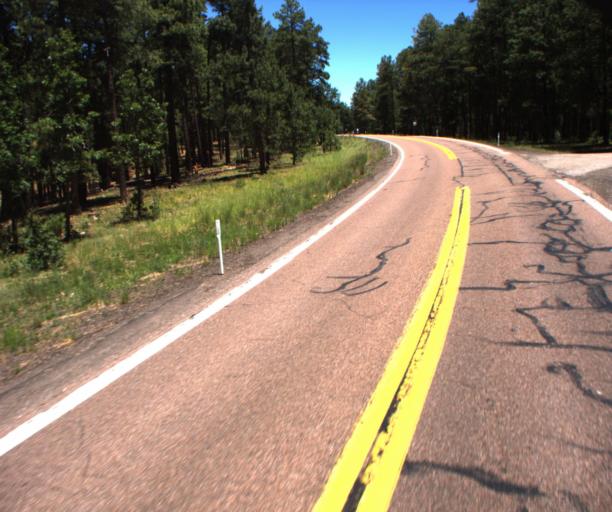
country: US
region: Arizona
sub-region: Gila County
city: Pine
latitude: 34.4508
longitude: -111.4182
